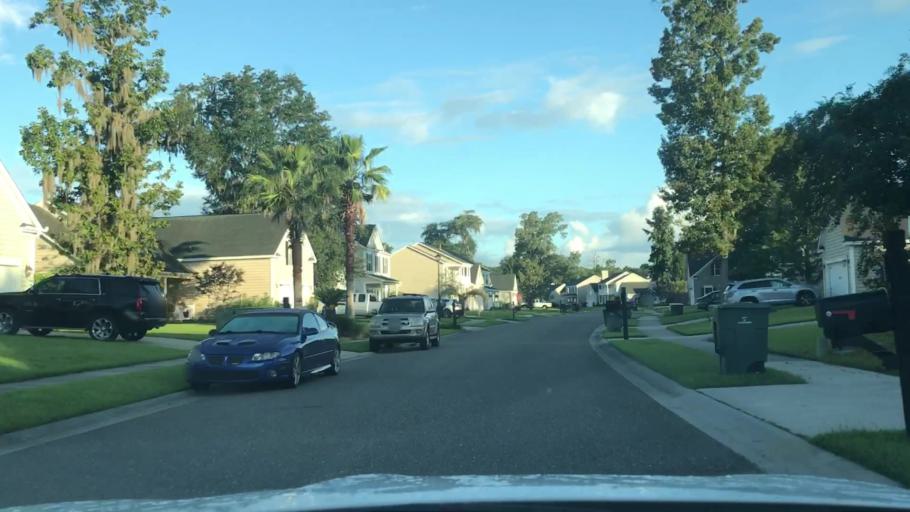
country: US
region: South Carolina
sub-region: Charleston County
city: Shell Point
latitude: 32.8326
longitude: -80.0988
